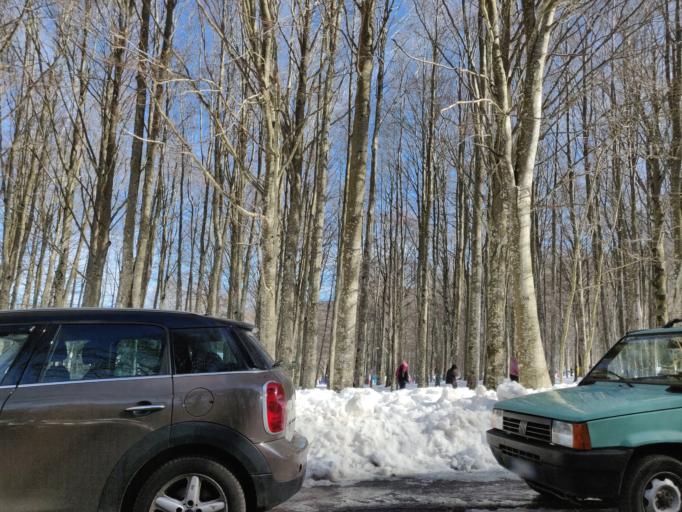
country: IT
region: Tuscany
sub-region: Provincia di Grosseto
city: Seggiano
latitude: 42.8902
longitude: 11.6053
